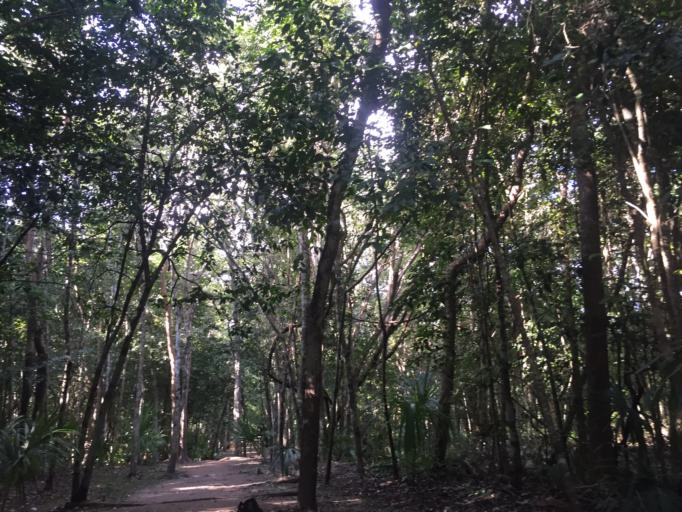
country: MX
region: Quintana Roo
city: Coba
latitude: 20.4842
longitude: -87.7228
